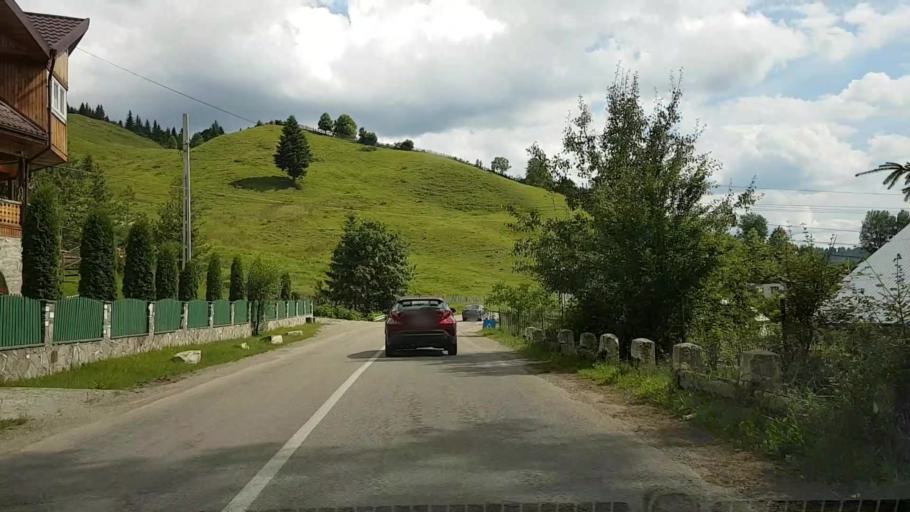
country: RO
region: Neamt
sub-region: Comuna Bicaz
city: Dodeni
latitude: 47.0046
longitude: 26.0980
